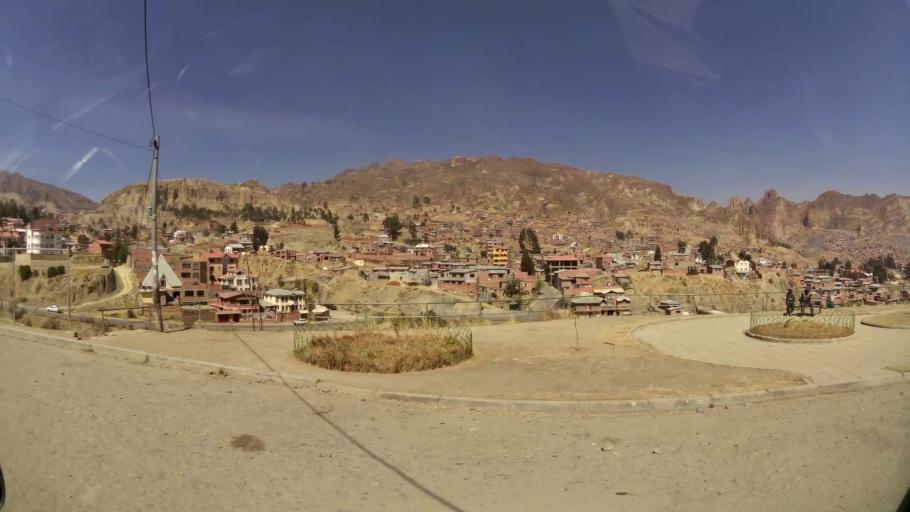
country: BO
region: La Paz
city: La Paz
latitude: -16.5383
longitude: -68.0453
